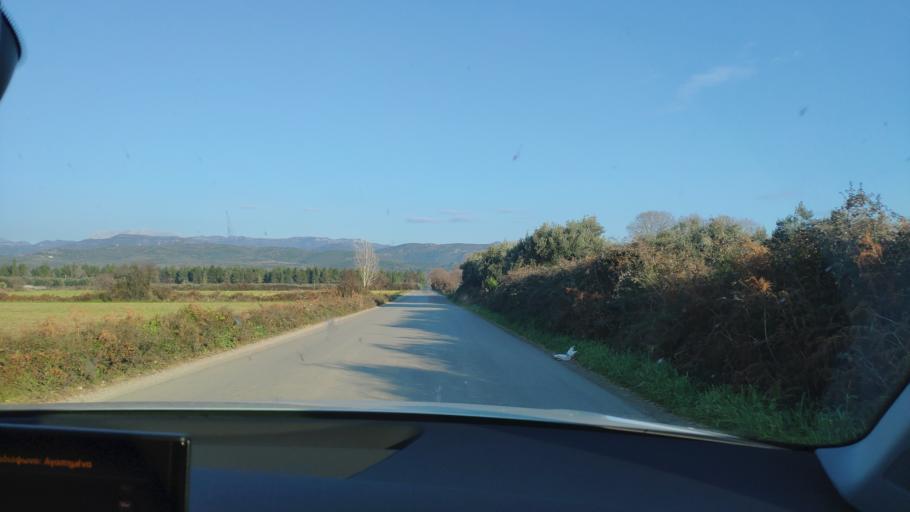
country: GR
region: West Greece
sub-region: Nomos Aitolias kai Akarnanias
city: Krikellos
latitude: 38.9303
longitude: 21.1622
